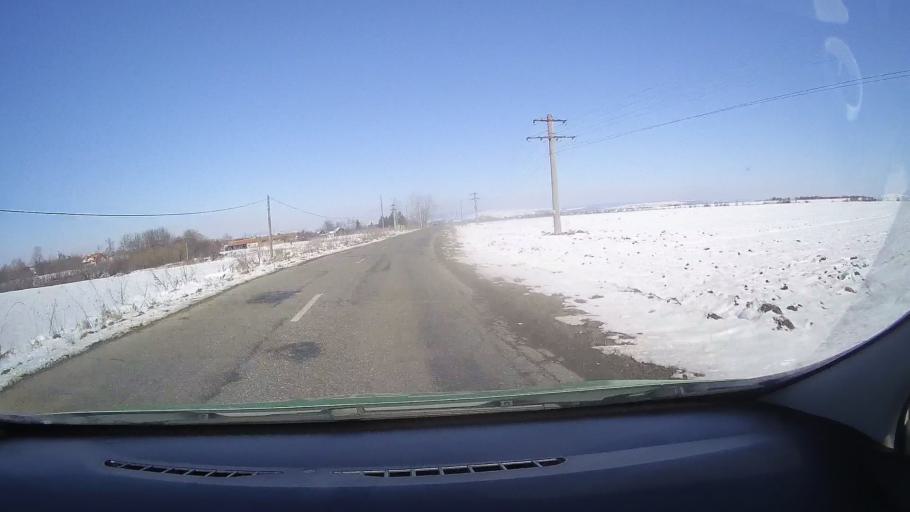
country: RO
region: Brasov
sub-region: Comuna Harseni
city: Harseni
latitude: 45.7781
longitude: 25.0010
